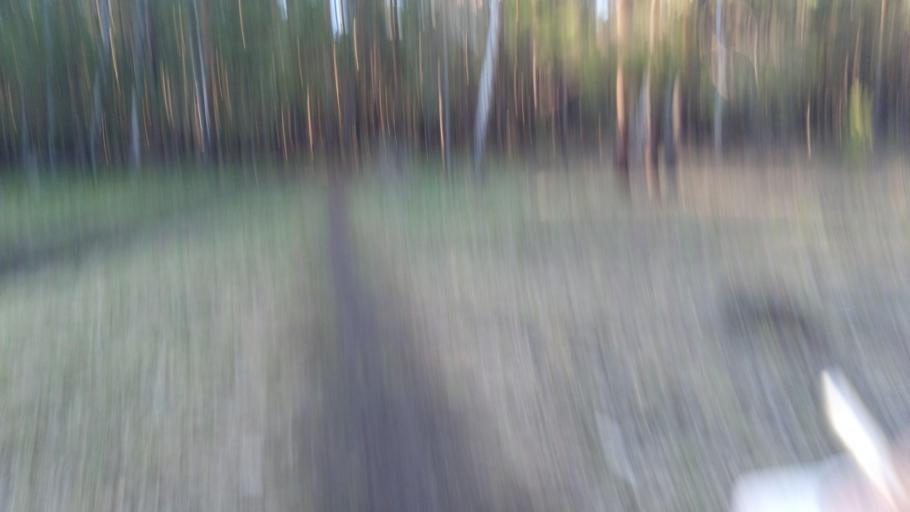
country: RU
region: Chelyabinsk
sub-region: Gorod Chelyabinsk
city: Chelyabinsk
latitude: 55.1277
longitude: 61.3396
